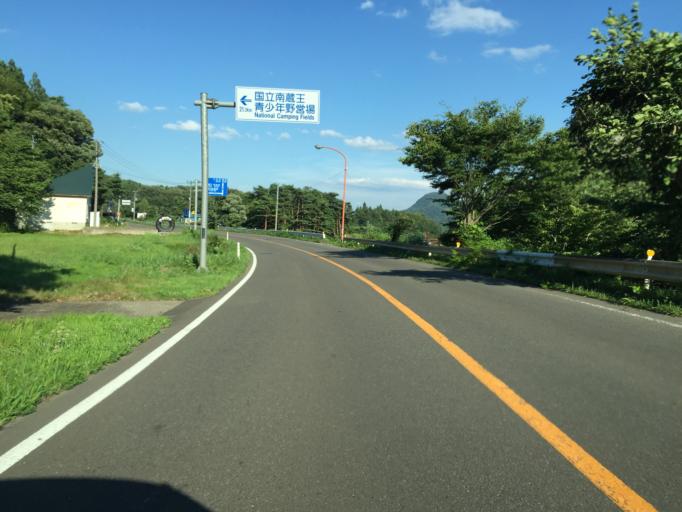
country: JP
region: Miyagi
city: Shiroishi
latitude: 37.9869
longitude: 140.4531
